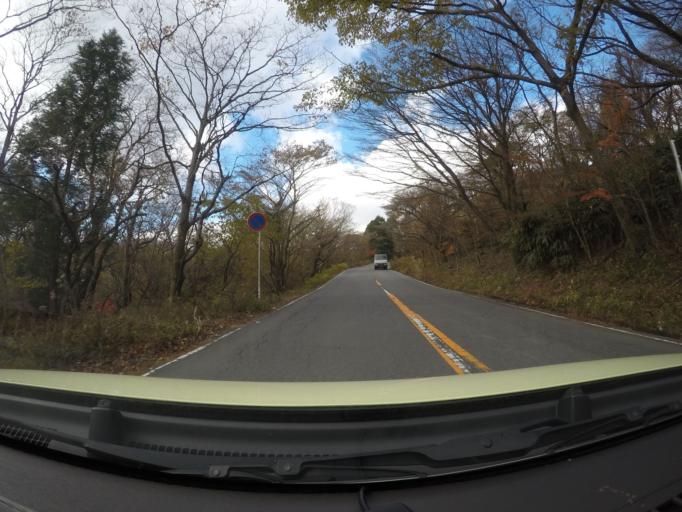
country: JP
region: Kanagawa
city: Hakone
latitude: 35.2110
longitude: 139.0133
